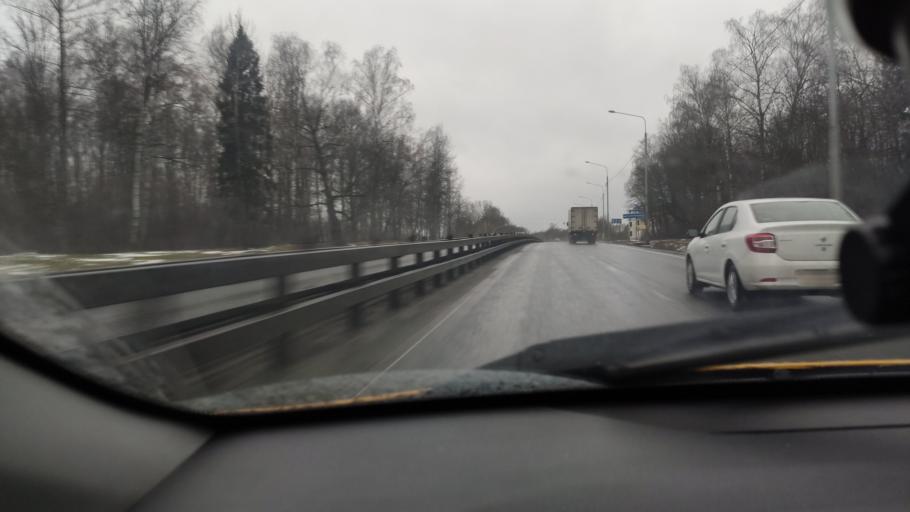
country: RU
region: Moskovskaya
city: Troitsk
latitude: 55.3124
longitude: 37.2354
